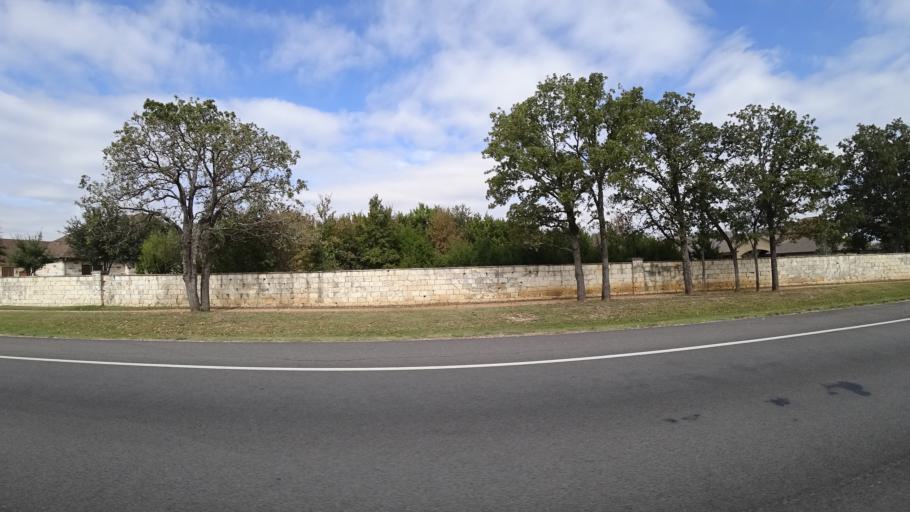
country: US
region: Texas
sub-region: Williamson County
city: Brushy Creek
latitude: 30.5320
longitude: -97.7133
